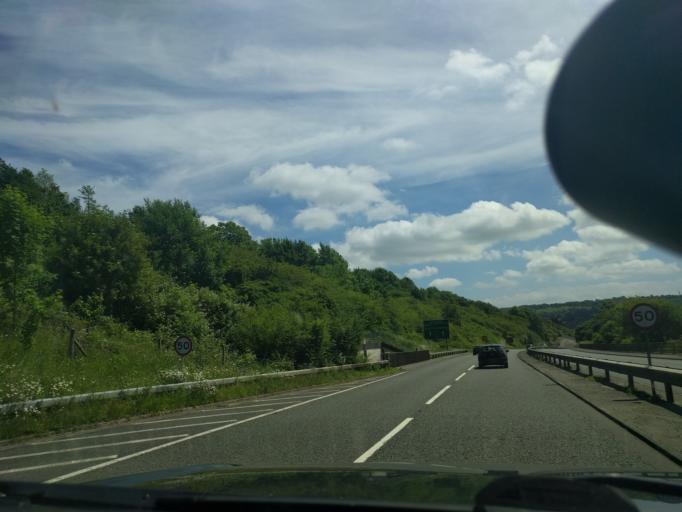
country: GB
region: England
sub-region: Bath and North East Somerset
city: Bath
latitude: 51.4073
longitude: -2.3415
